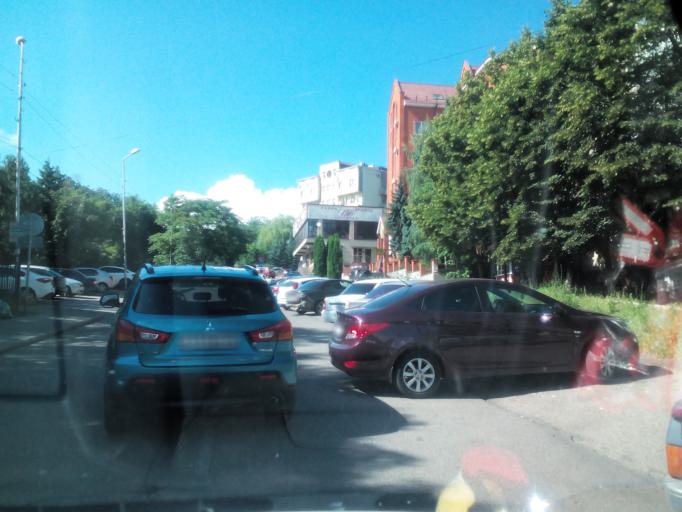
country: RU
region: Stavropol'skiy
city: Pyatigorsk
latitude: 44.0472
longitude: 43.0686
